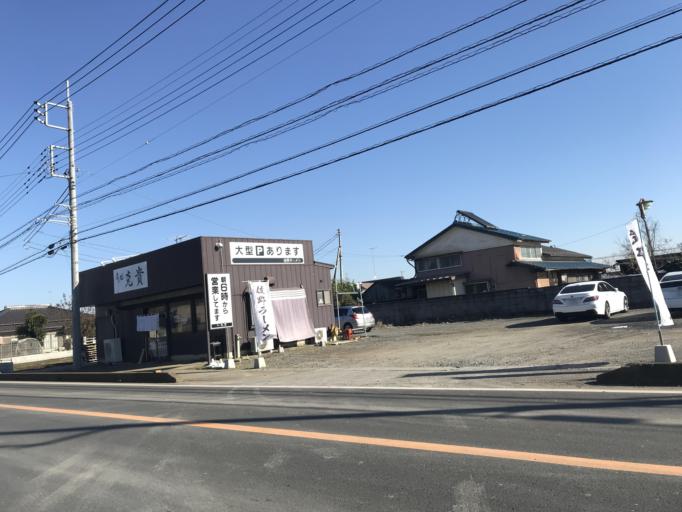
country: JP
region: Tochigi
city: Oyama
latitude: 36.2271
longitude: 139.8239
